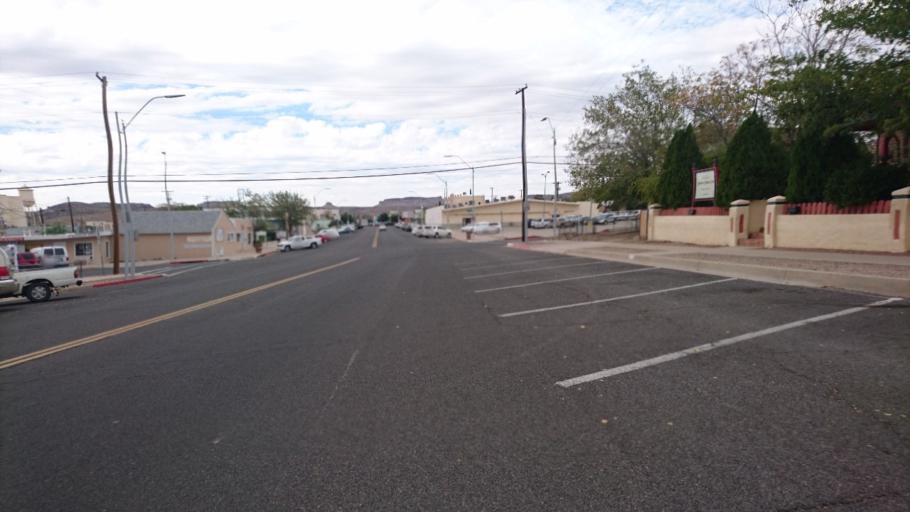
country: US
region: Arizona
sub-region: Mohave County
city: Kingman
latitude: 35.1890
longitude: -114.0486
